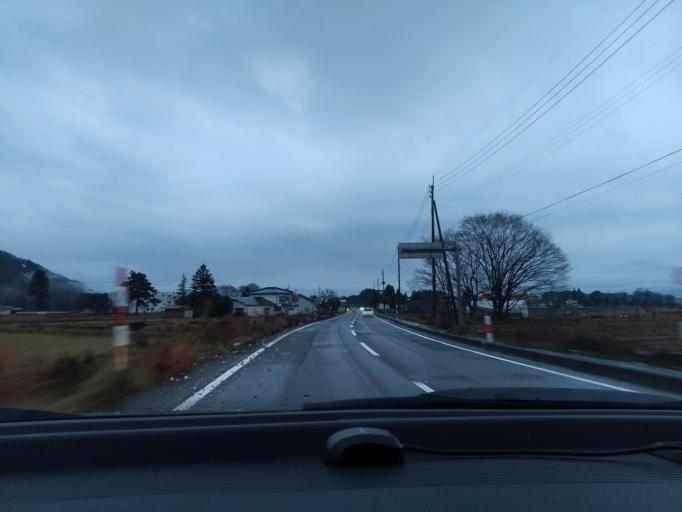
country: JP
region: Akita
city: Kakunodatemachi
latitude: 39.6138
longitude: 140.6297
